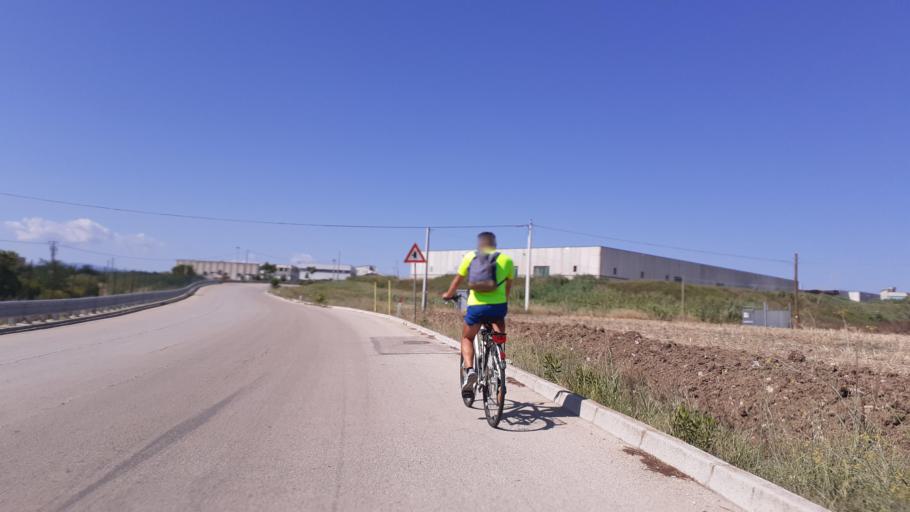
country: IT
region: Abruzzo
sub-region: Provincia di Chieti
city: Vasto
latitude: 42.1704
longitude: 14.7043
